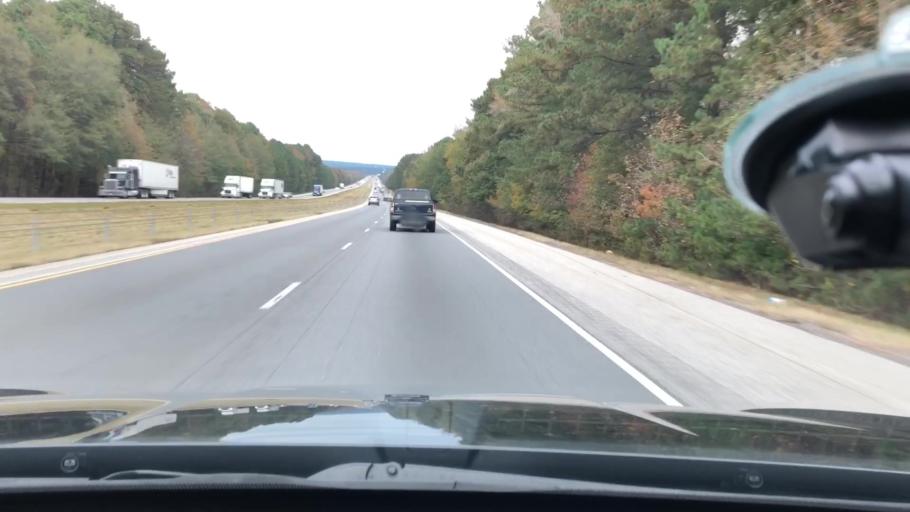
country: US
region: Arkansas
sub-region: Clark County
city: Arkadelphia
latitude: 34.1454
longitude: -93.0794
